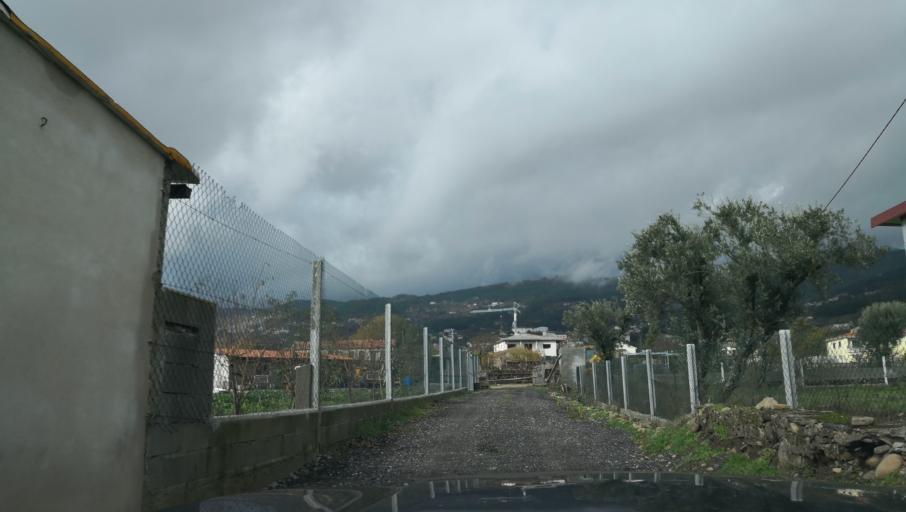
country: PT
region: Vila Real
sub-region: Vila Real
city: Vila Real
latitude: 41.3146
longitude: -7.7572
